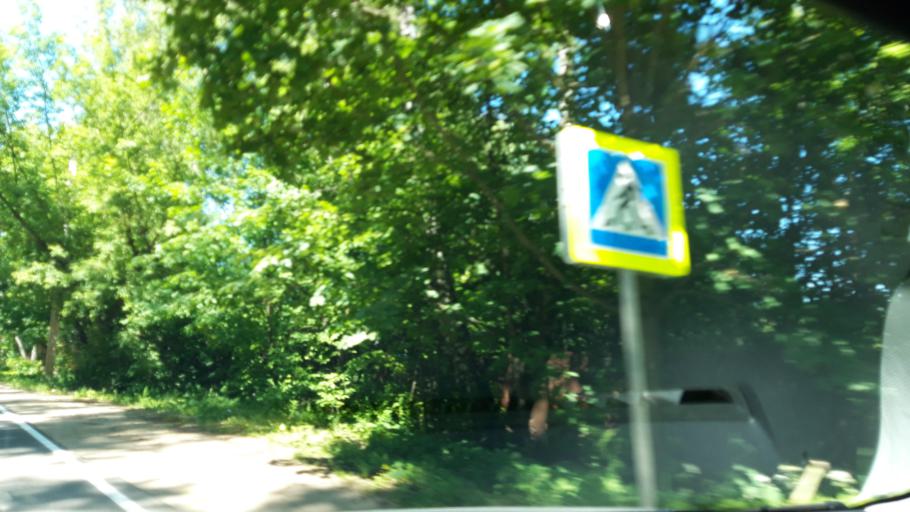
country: RU
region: Moskovskaya
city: Solnechnogorsk
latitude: 56.1666
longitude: 36.9636
